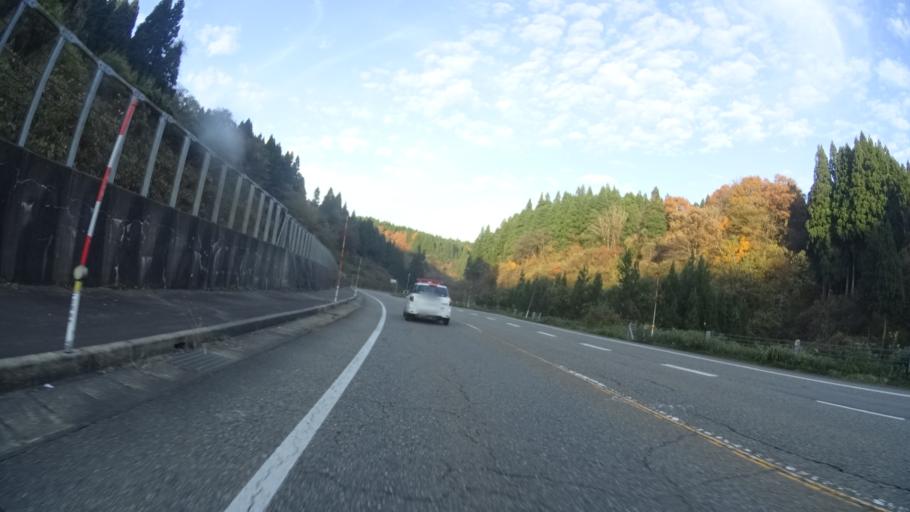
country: JP
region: Niigata
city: Kashiwazaki
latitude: 37.4101
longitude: 138.6721
